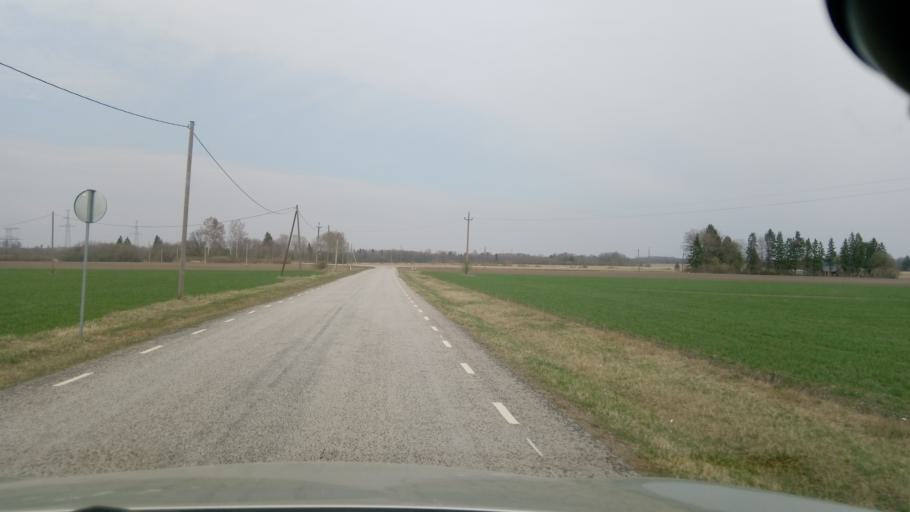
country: EE
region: Jaervamaa
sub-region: Tueri vald
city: Tueri
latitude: 58.7904
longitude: 25.4769
